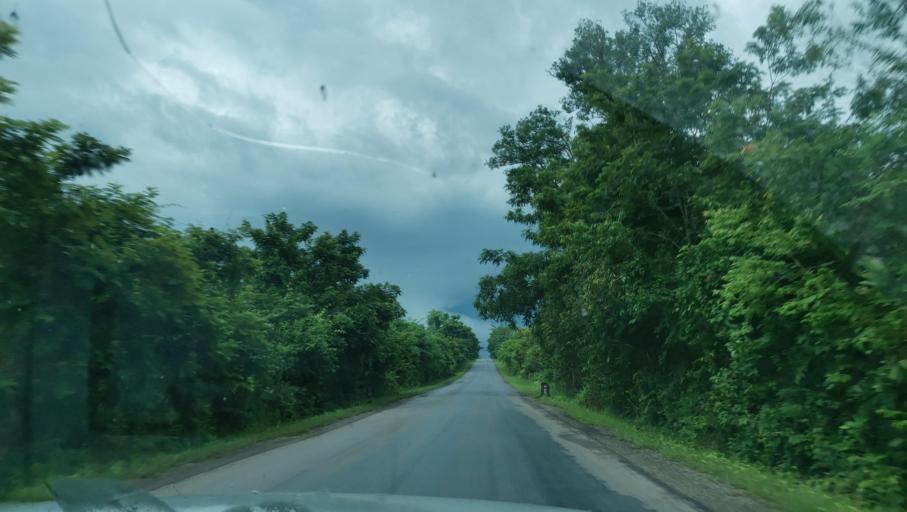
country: TH
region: Nakhon Phanom
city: Ban Phaeng
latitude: 17.8864
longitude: 104.4011
